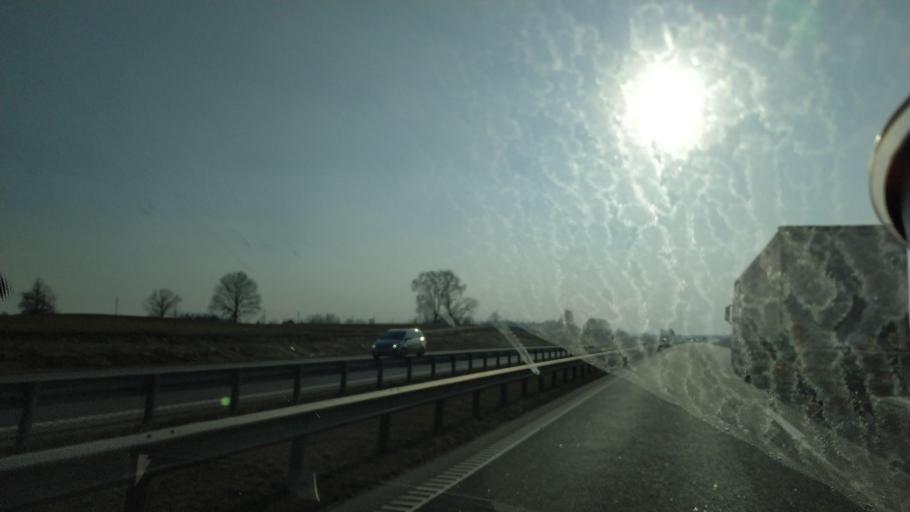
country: LT
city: Ezerelis
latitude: 54.7201
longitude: 23.6634
